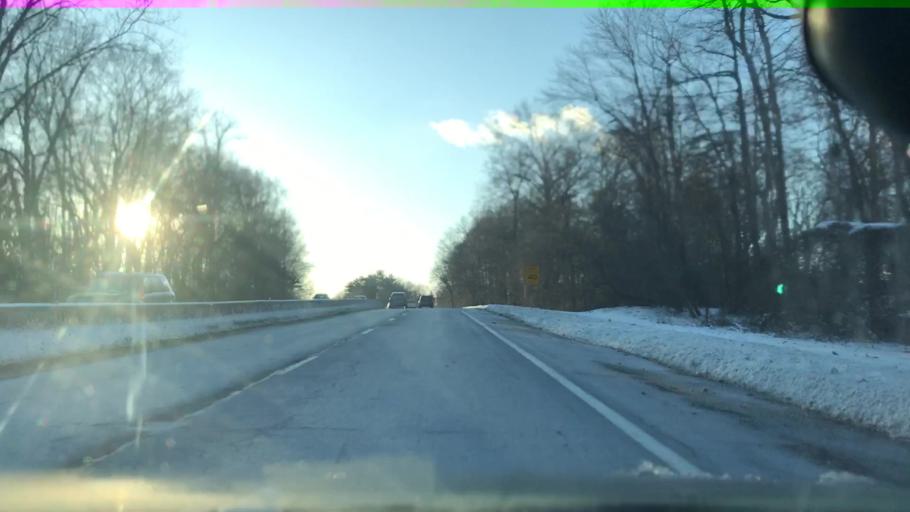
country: US
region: New York
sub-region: Westchester County
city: Tuckahoe
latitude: 40.9610
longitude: -73.7911
